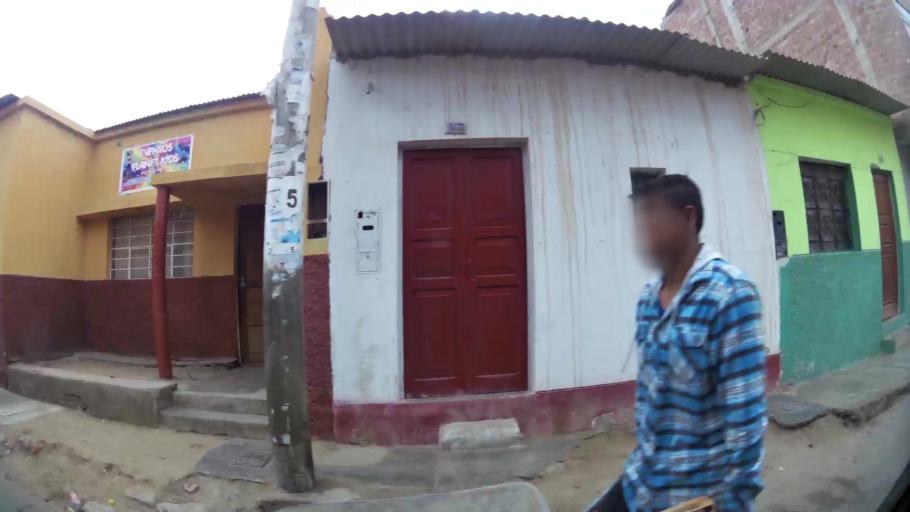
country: PE
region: La Libertad
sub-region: Provincia de Trujillo
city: La Esperanza
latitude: -8.0819
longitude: -79.0459
